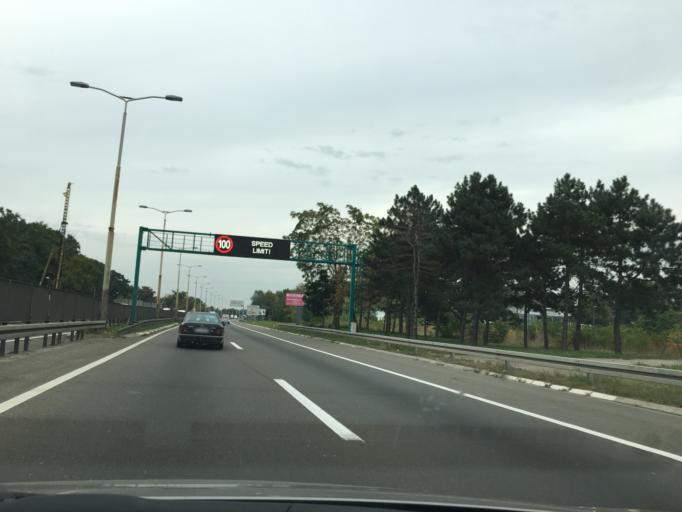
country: RS
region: Central Serbia
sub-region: Belgrade
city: Zemun
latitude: 44.8291
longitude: 20.3830
